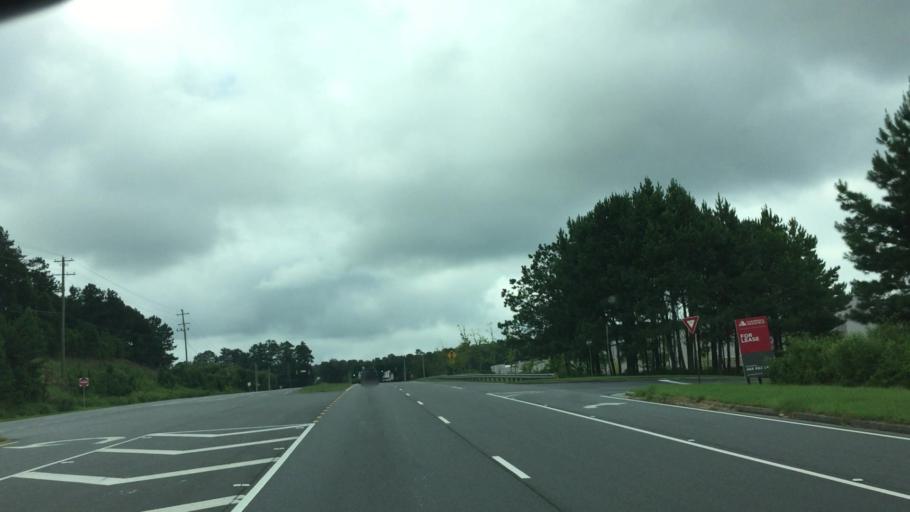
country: US
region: Georgia
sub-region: Fulton County
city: Johns Creek
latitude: 34.1042
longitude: -84.2169
